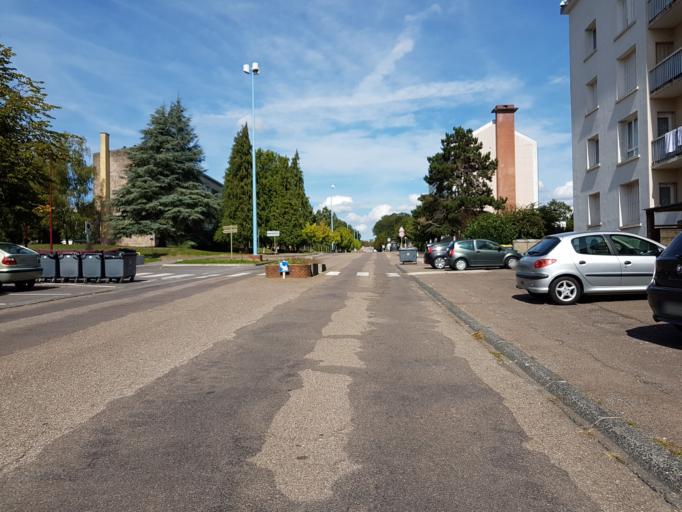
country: FR
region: Franche-Comte
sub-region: Departement de la Haute-Saone
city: Luxeuil-les-Bains
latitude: 47.8172
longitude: 6.3628
